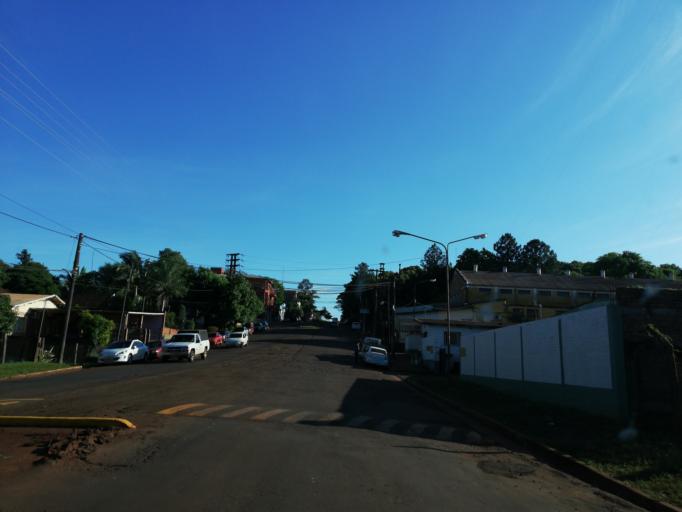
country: AR
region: Misiones
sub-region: Departamento de Obera
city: Obera
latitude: -27.4976
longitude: -55.1173
